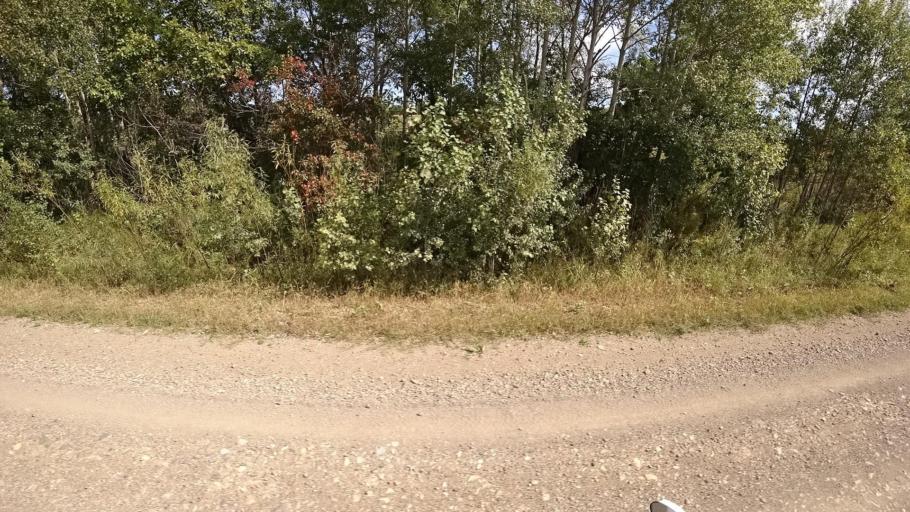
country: RU
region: Primorskiy
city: Yakovlevka
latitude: 44.7197
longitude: 133.6157
